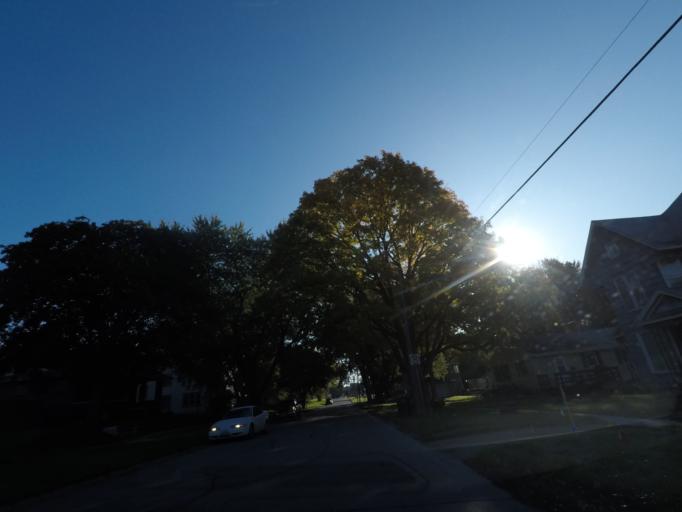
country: US
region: Iowa
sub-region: Story County
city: Nevada
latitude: 42.0196
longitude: -93.4562
